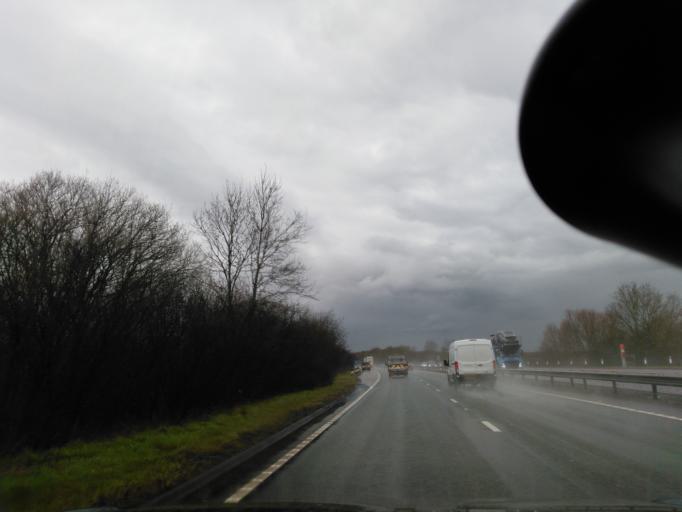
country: GB
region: England
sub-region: North Yorkshire
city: Thirsk
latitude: 54.2365
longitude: -1.3272
